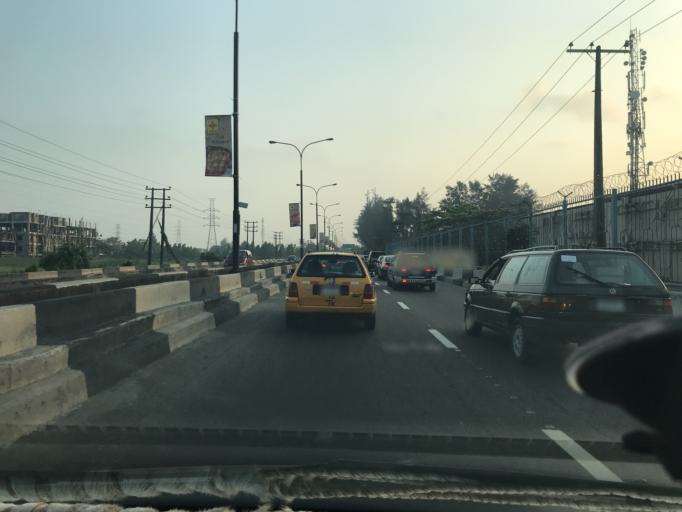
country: NG
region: Lagos
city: Lagos
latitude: 6.4595
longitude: 3.4131
